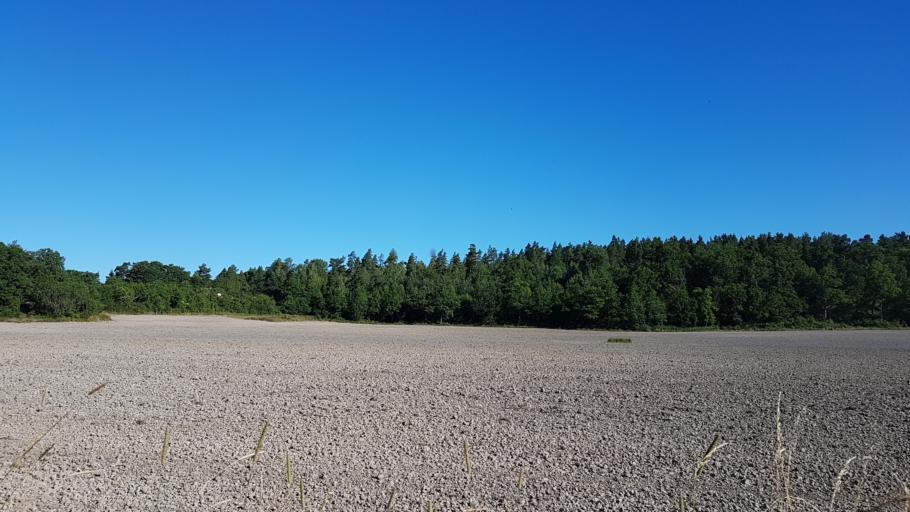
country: SE
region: OEstergoetland
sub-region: Valdemarsviks Kommun
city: Gusum
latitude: 58.4291
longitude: 16.5786
